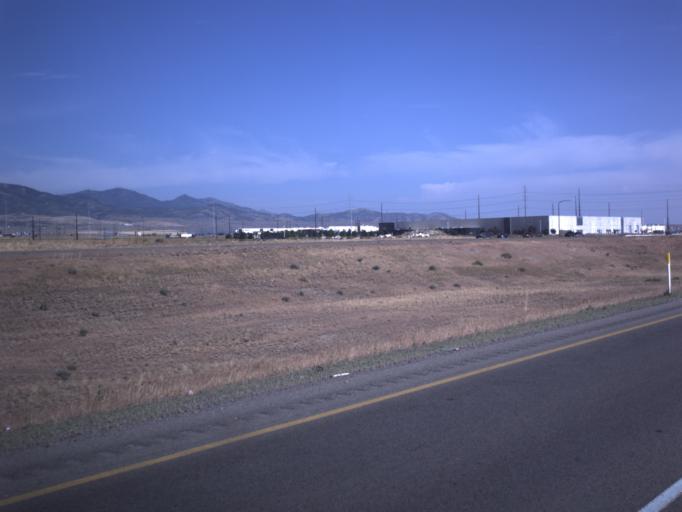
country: US
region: Utah
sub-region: Salt Lake County
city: Herriman
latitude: 40.5578
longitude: -112.0310
